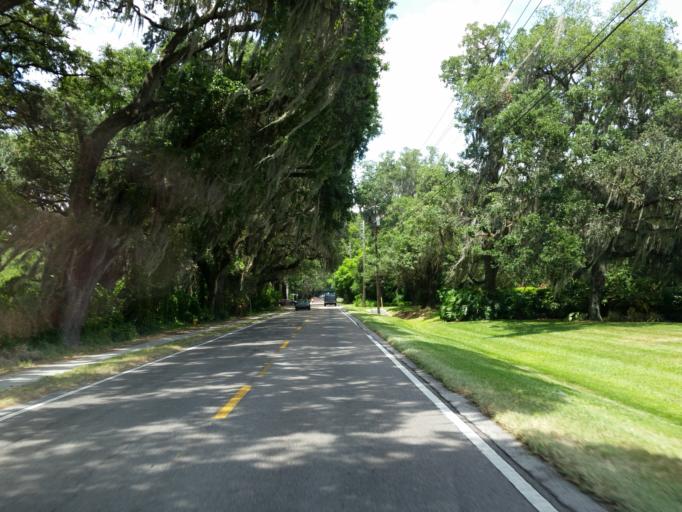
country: US
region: Florida
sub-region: Hillsborough County
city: Valrico
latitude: 27.9560
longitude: -82.2528
